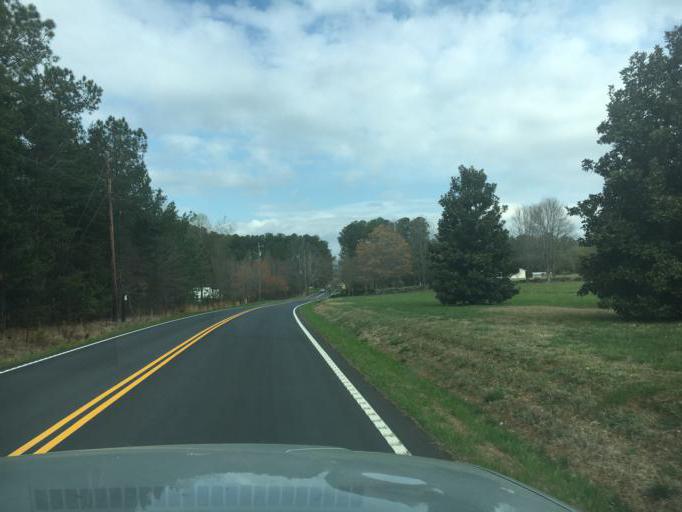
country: US
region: South Carolina
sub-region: Spartanburg County
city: Landrum
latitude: 35.1035
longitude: -82.2100
